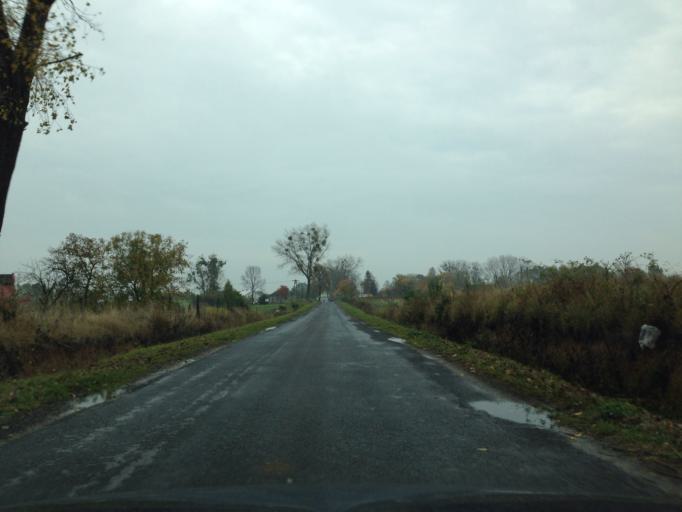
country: PL
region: Kujawsko-Pomorskie
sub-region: Powiat brodnicki
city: Swiedziebnia
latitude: 53.1563
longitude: 19.5132
